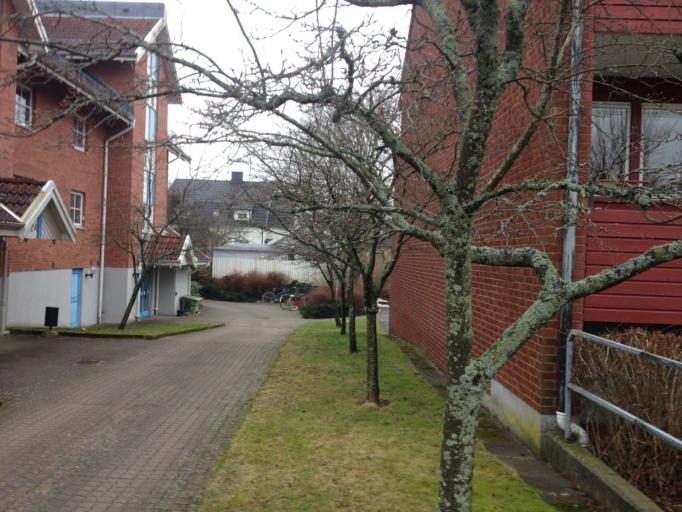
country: SE
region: Kronoberg
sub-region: Markaryds Kommun
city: Markaryd
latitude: 56.4598
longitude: 13.5931
